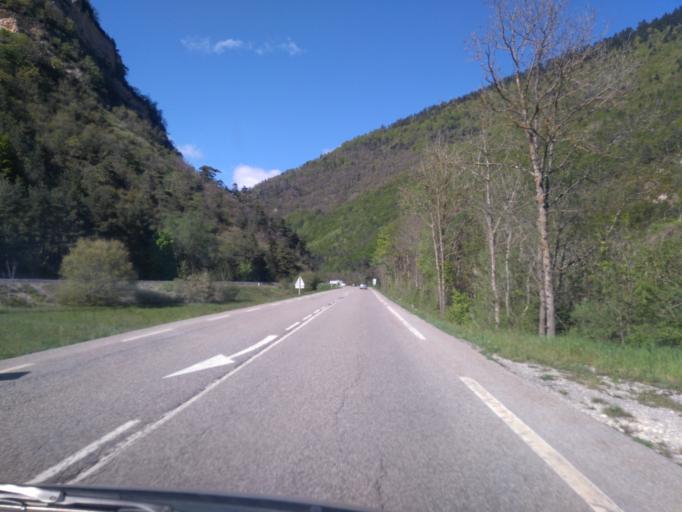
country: FR
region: Provence-Alpes-Cote d'Azur
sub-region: Departement des Hautes-Alpes
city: Veynes
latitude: 44.6425
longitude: 5.6998
